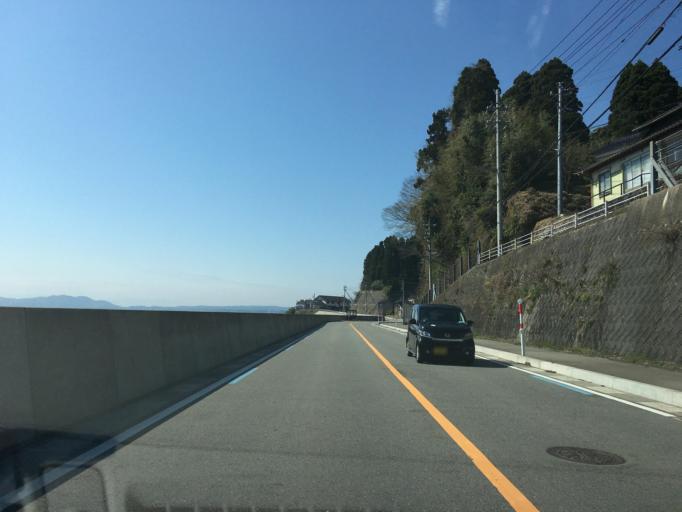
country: JP
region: Toyama
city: Himi
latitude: 36.9024
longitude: 137.0126
